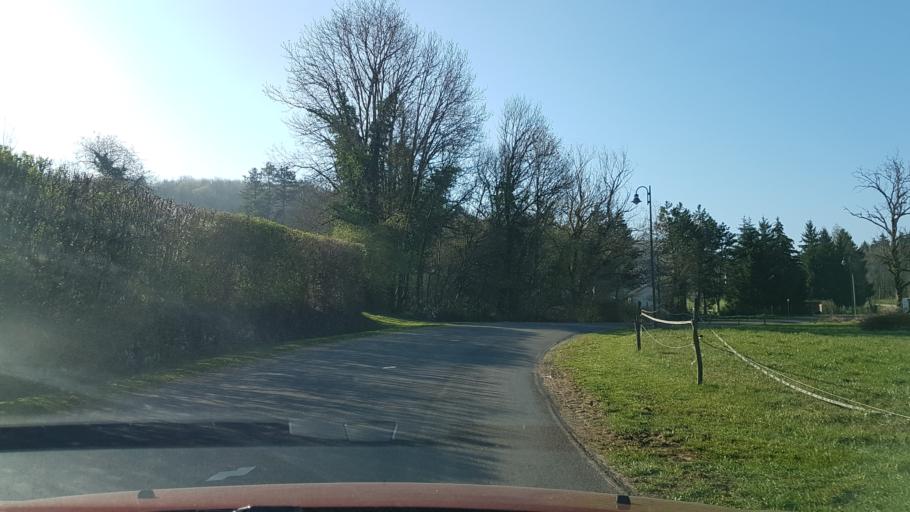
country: FR
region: Franche-Comte
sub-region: Departement du Jura
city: Orgelet
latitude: 46.4999
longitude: 5.5053
